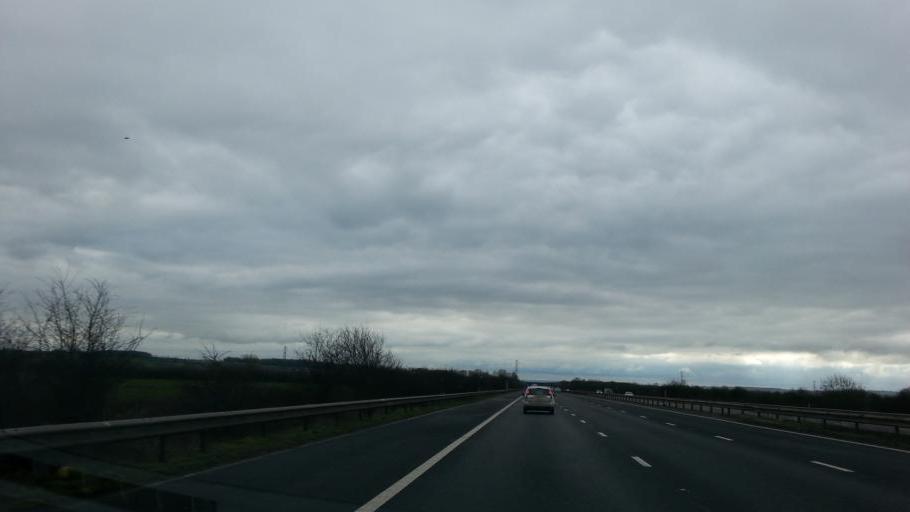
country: GB
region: England
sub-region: Somerset
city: Puriton
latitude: 51.1923
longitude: -2.9714
